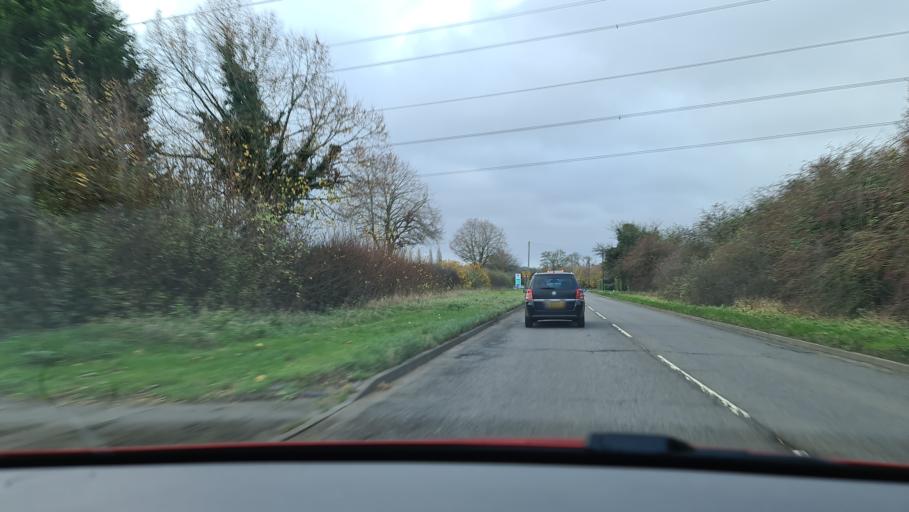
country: GB
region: England
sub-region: Buckinghamshire
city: Weston Turville
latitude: 51.7725
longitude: -0.7884
